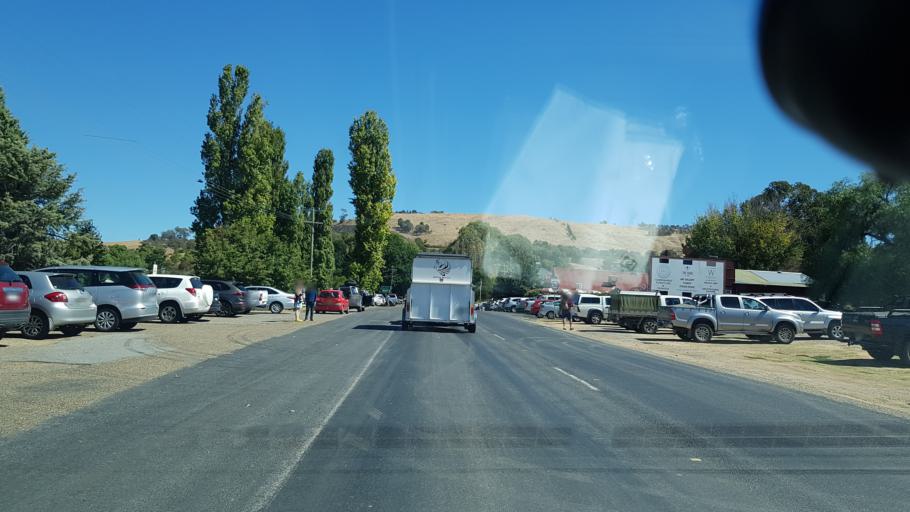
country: AU
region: New South Wales
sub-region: Gundagai
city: Gundagai
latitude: -34.8233
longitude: 148.3265
